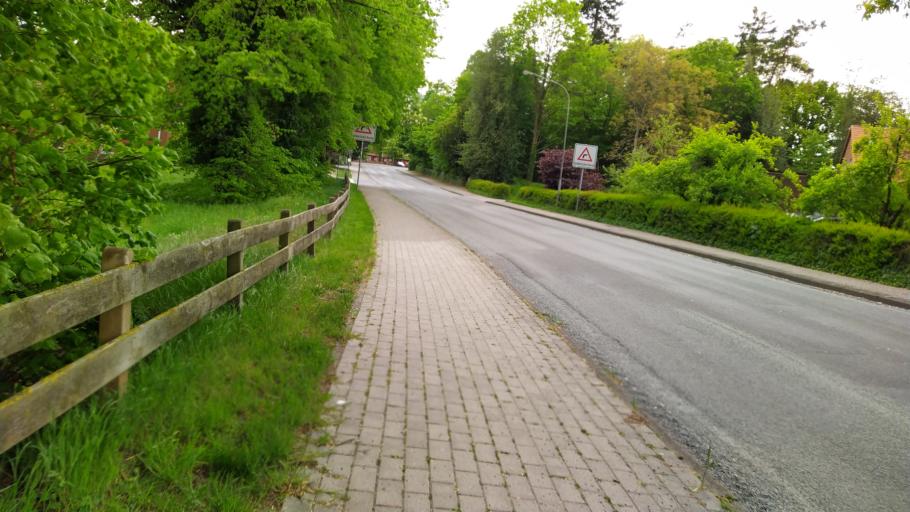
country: DE
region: Lower Saxony
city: Kirchtimke
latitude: 53.2525
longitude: 9.1523
